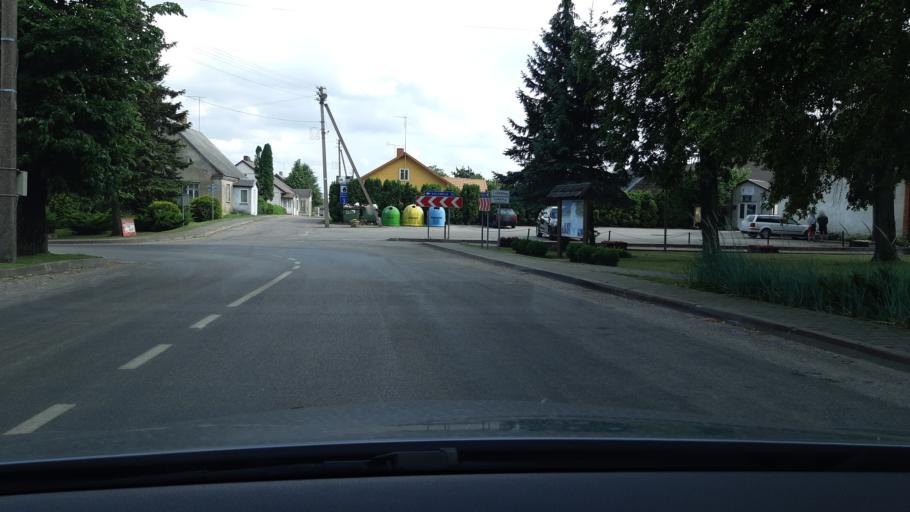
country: LT
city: Kybartai
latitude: 54.4545
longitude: 22.7109
